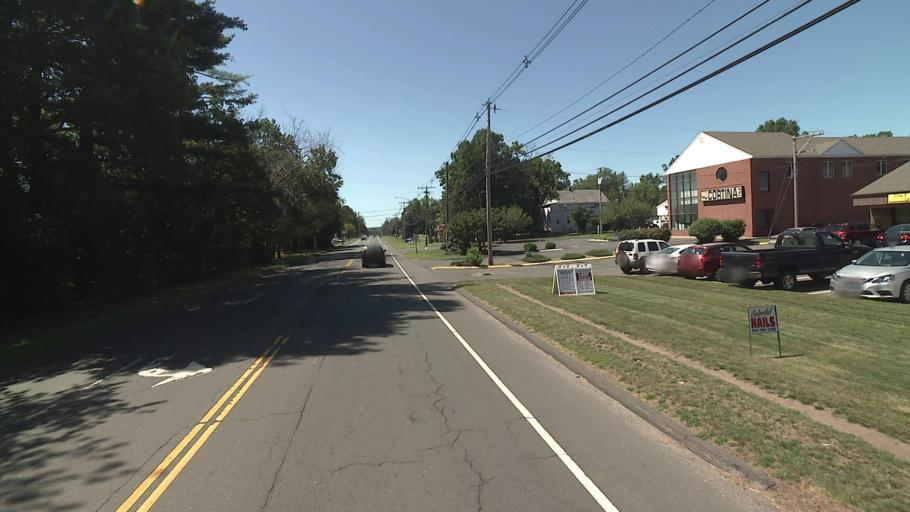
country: US
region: Connecticut
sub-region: Hartford County
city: Plainville
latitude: 41.6574
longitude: -72.8673
